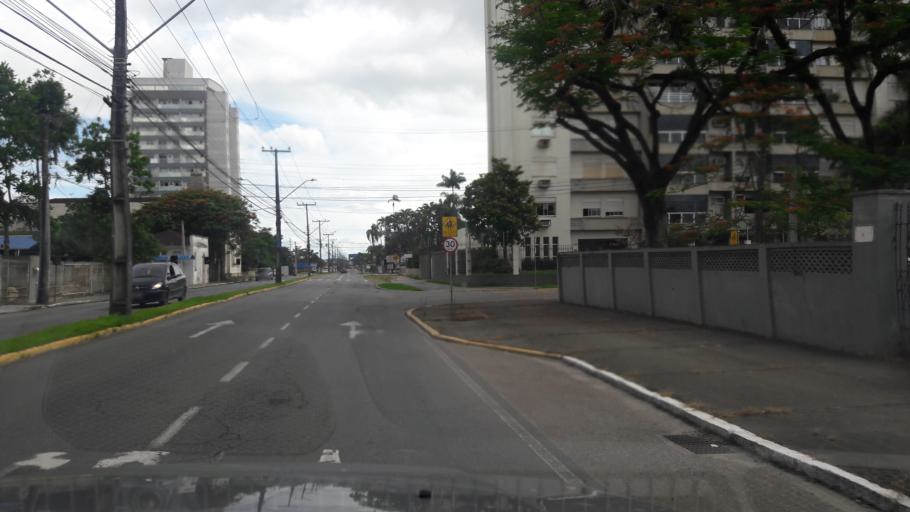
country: BR
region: Santa Catarina
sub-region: Joinville
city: Joinville
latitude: -26.3116
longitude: -48.8408
